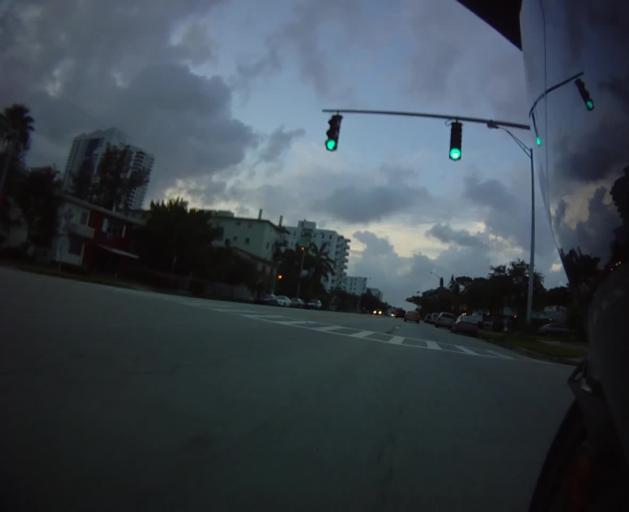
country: US
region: Florida
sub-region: Miami-Dade County
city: Miami Beach
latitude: 25.7828
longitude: -80.1409
